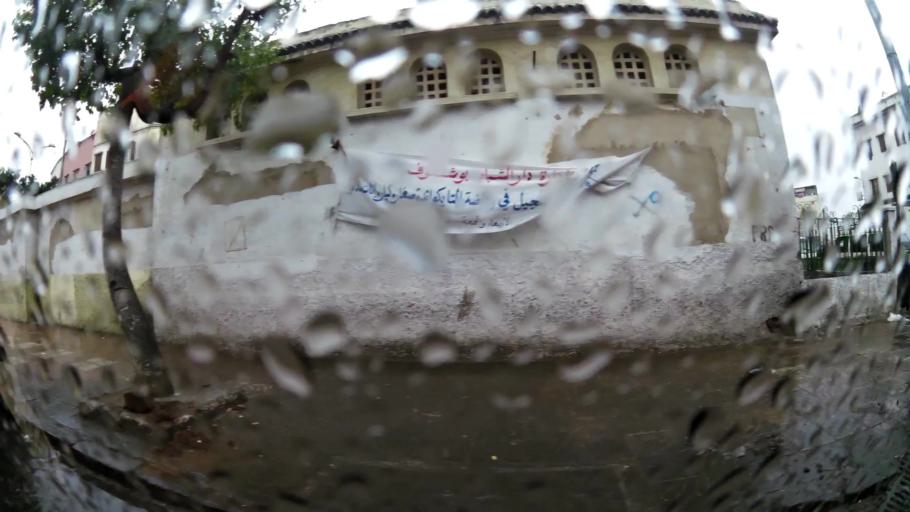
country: MA
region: Grand Casablanca
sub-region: Casablanca
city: Casablanca
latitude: 33.5713
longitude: -7.6049
